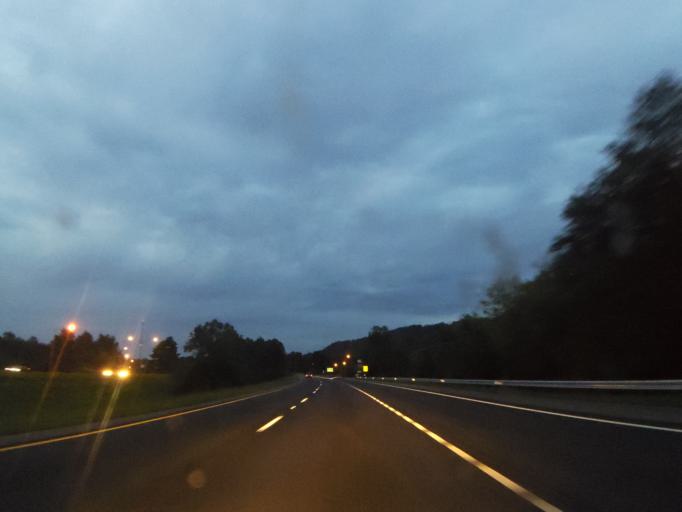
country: US
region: Alabama
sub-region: DeKalb County
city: Collinsville
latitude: 34.2716
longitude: -85.8816
